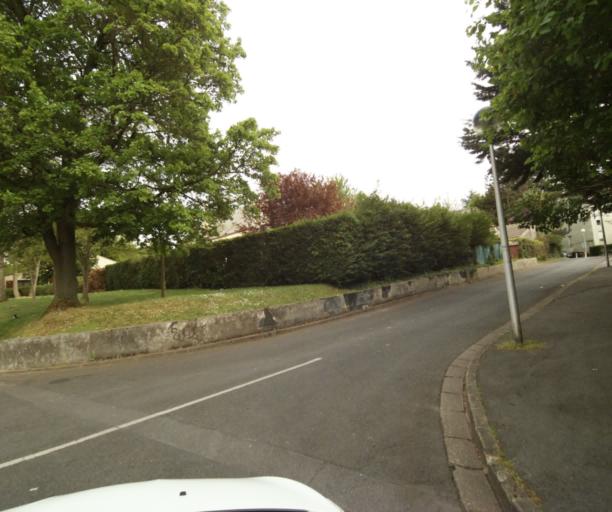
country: FR
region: Ile-de-France
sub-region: Departement de Seine-et-Marne
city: Noisiel
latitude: 48.8540
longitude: 2.6320
